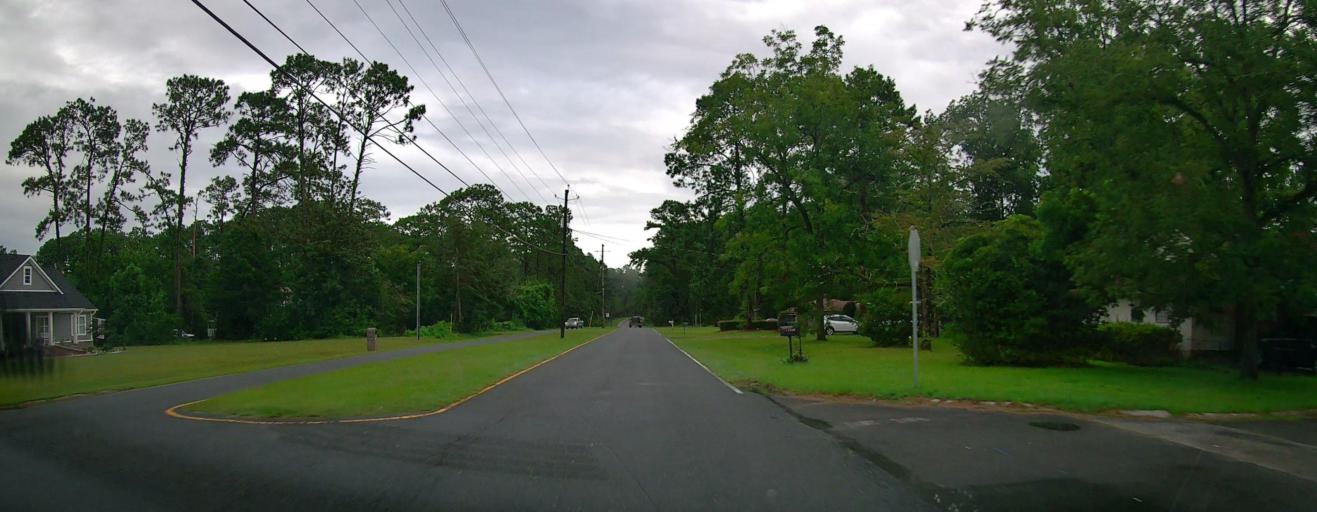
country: US
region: Georgia
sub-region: Ware County
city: Deenwood
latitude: 31.2306
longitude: -82.3850
